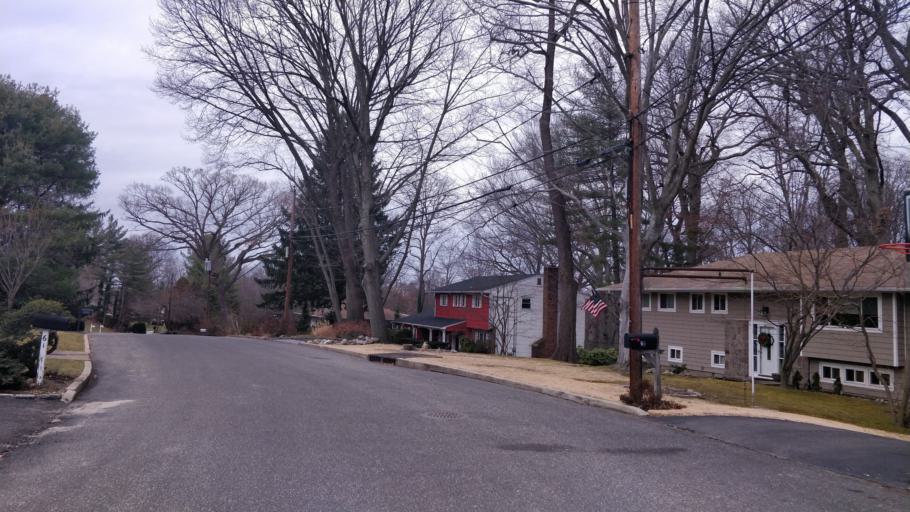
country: US
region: New York
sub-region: Nassau County
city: Locust Valley
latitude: 40.8813
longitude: -73.6189
